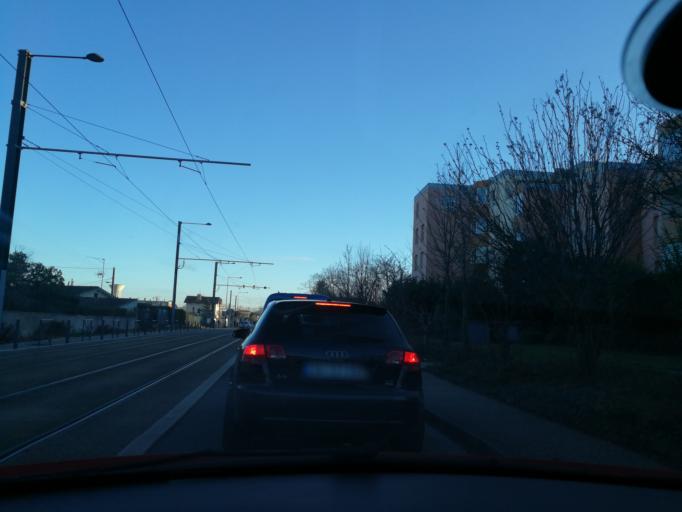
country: FR
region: Midi-Pyrenees
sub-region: Departement de la Haute-Garonne
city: Blagnac
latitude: 43.6321
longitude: 1.3915
